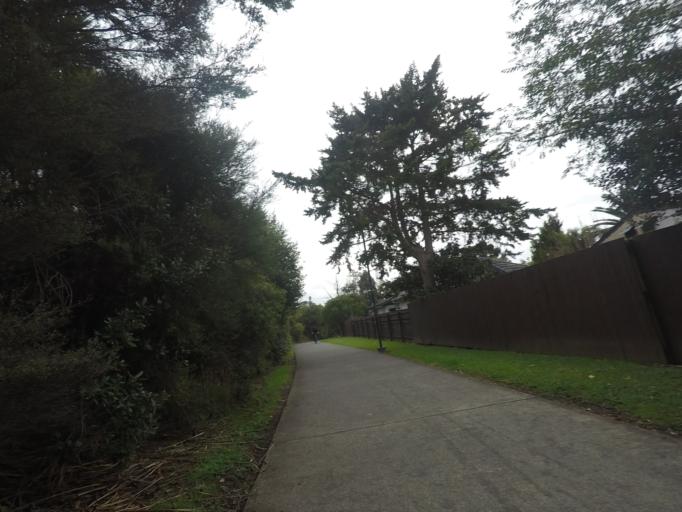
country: NZ
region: Auckland
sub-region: Auckland
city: Waitakere
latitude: -36.8953
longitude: 174.6323
